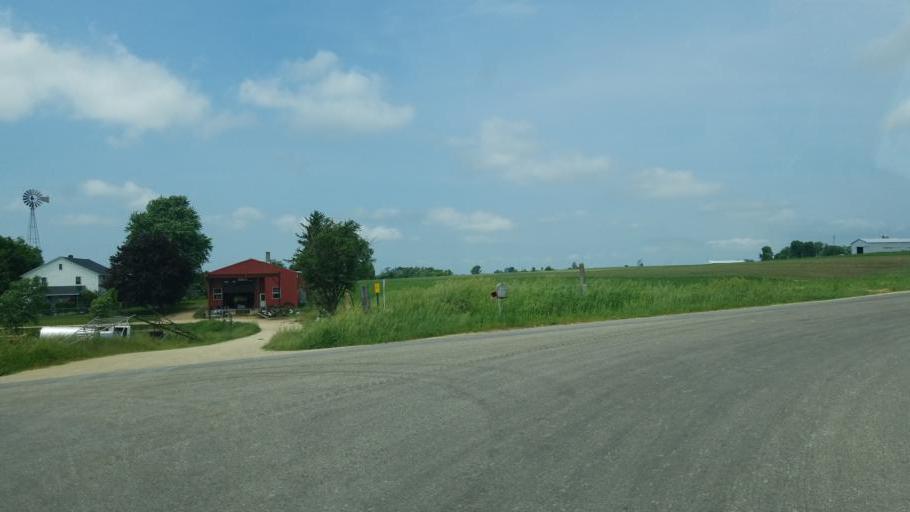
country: US
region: Wisconsin
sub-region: Monroe County
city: Cashton
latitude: 43.7110
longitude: -90.7101
